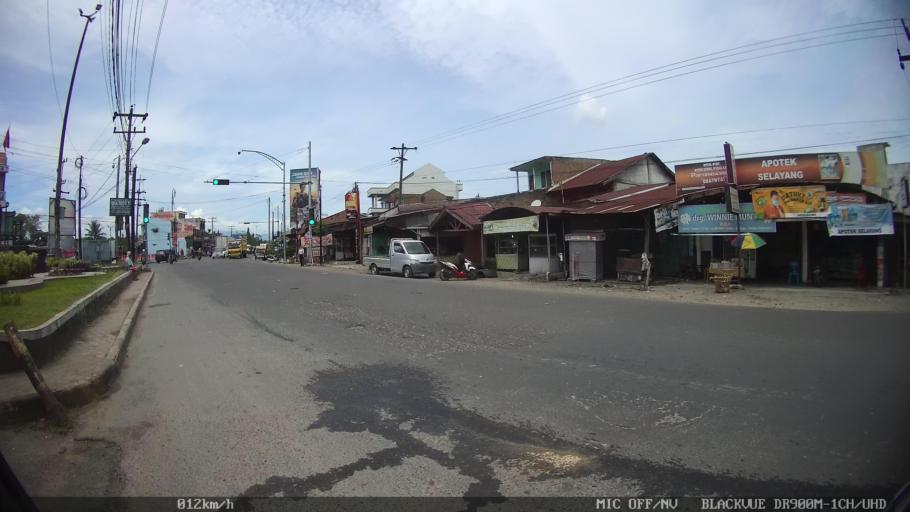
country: ID
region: North Sumatra
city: Sunggal
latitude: 3.5209
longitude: 98.6194
